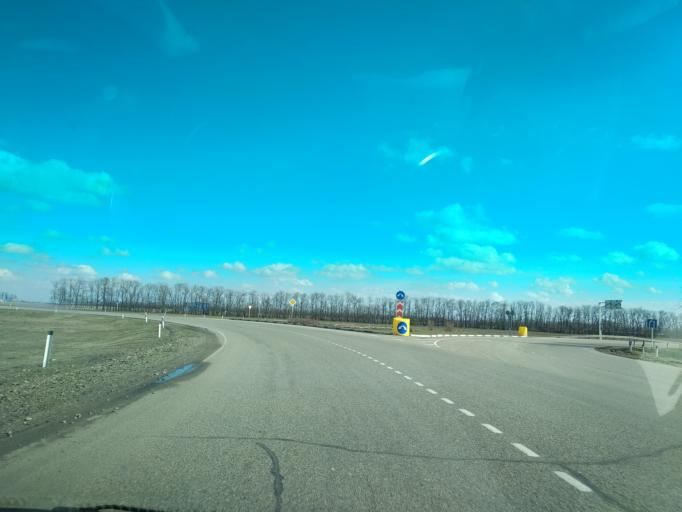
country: RU
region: Krasnodarskiy
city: Vyselki
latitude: 45.6152
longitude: 39.6341
